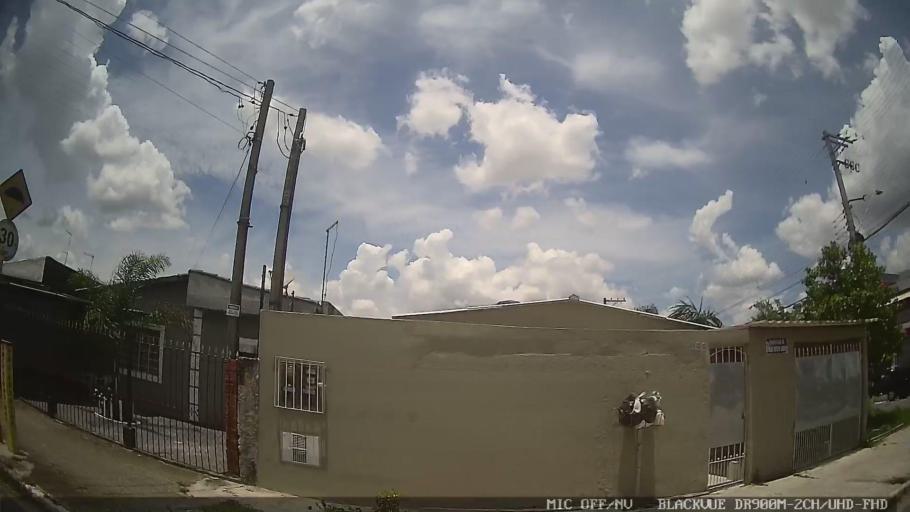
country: BR
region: Sao Paulo
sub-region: Suzano
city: Suzano
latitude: -23.5400
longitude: -46.3226
